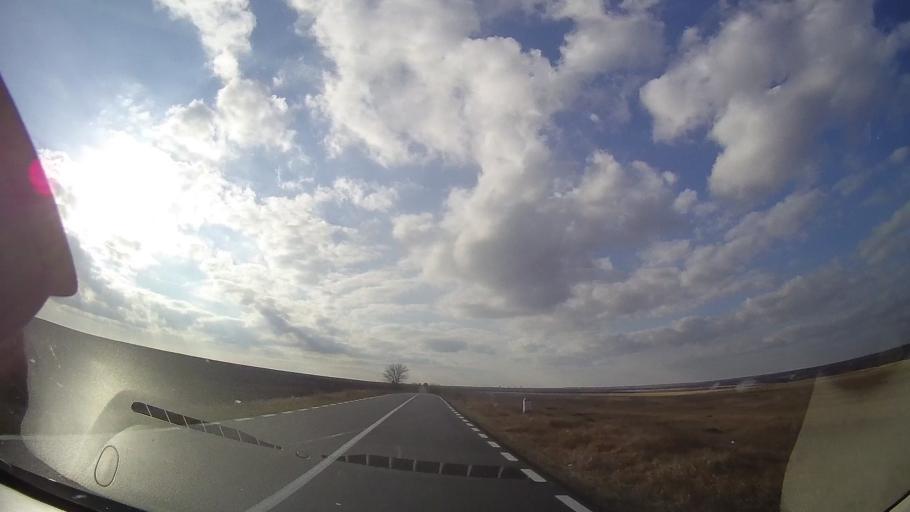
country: RO
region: Constanta
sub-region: Comuna Albesti
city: Albesti
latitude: 43.8085
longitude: 28.4037
